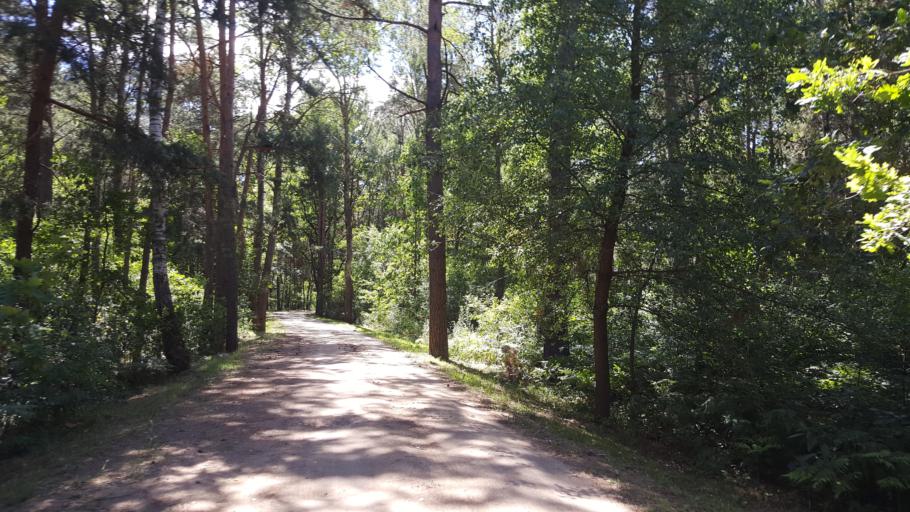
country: BY
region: Brest
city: Kamyanyets
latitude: 52.3295
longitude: 23.9015
